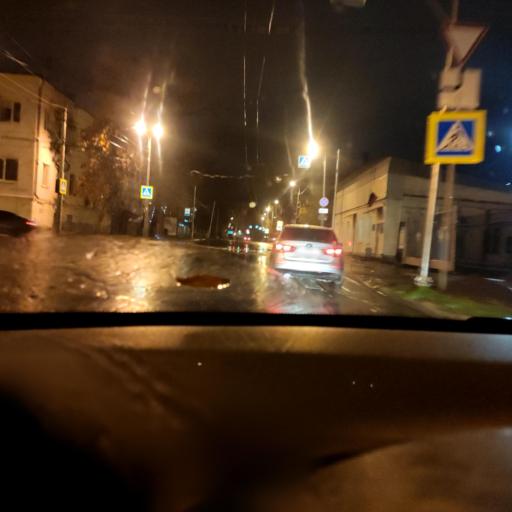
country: RU
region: Samara
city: Samara
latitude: 53.1981
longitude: 50.1270
